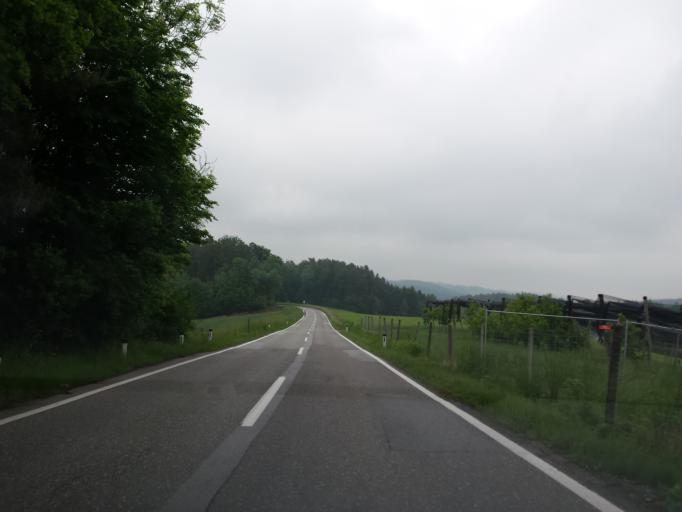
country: AT
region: Styria
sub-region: Politischer Bezirk Graz-Umgebung
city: Kumberg
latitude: 47.1434
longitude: 15.5299
